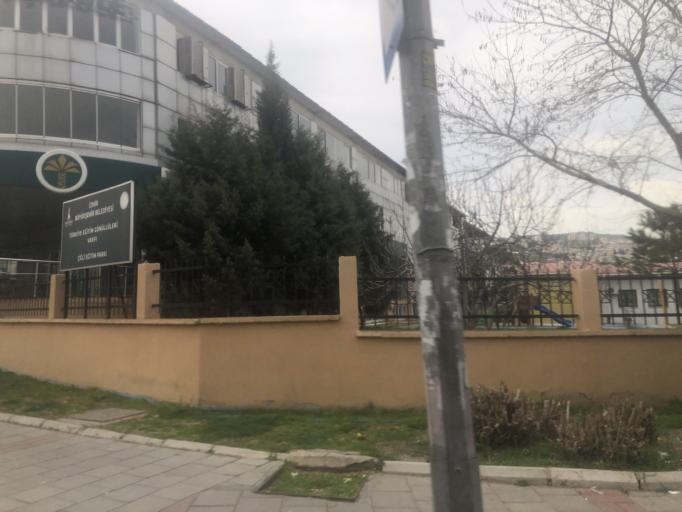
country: TR
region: Izmir
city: Karsiyaka
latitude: 38.4903
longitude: 27.0682
